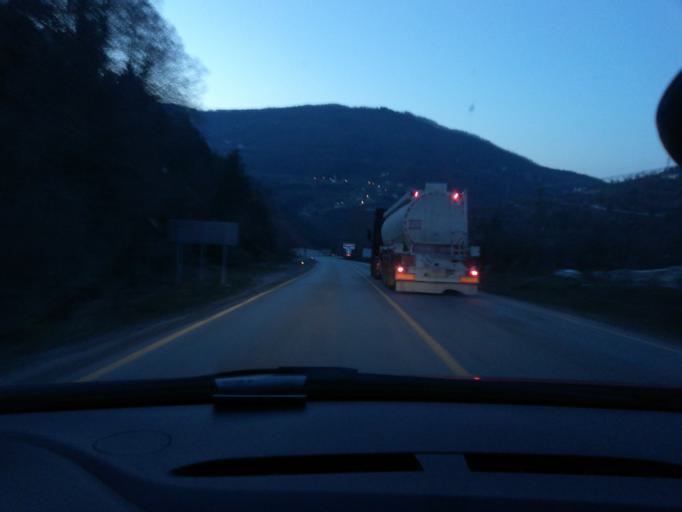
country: TR
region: Kastamonu
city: Inebolu
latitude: 41.9505
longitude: 33.7561
